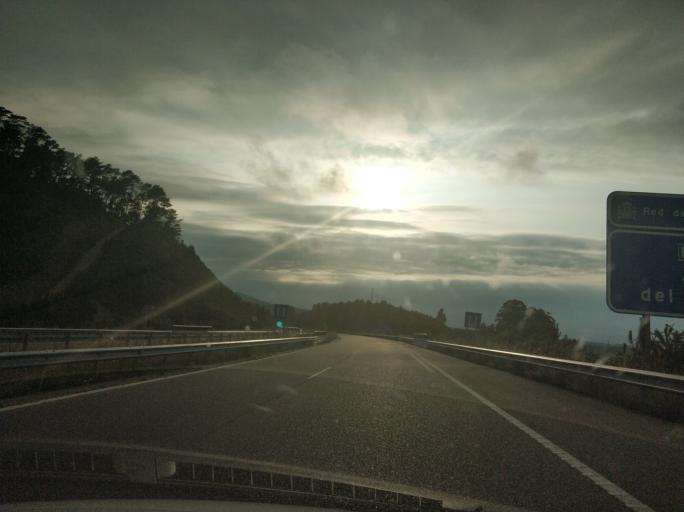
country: ES
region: Asturias
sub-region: Province of Asturias
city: Cudillero
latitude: 43.5581
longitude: -6.1762
